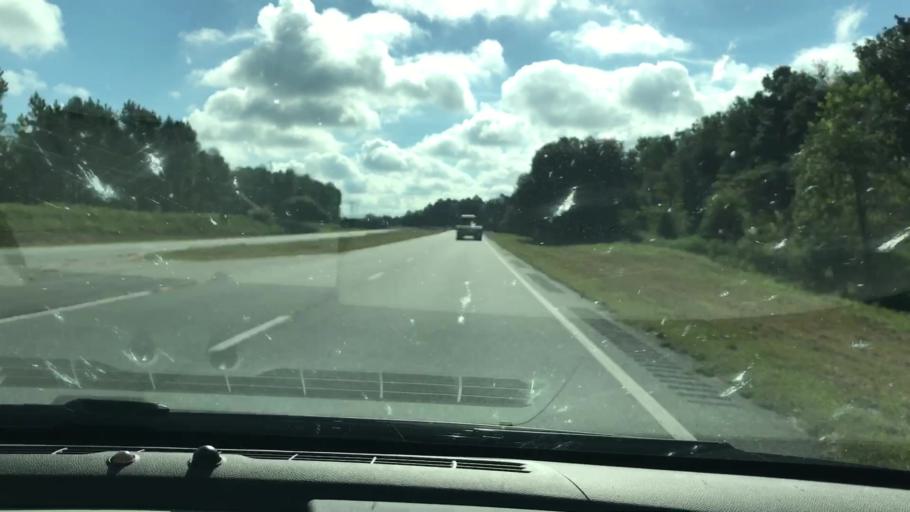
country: US
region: Georgia
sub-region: Worth County
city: Sylvester
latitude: 31.5511
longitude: -83.9716
